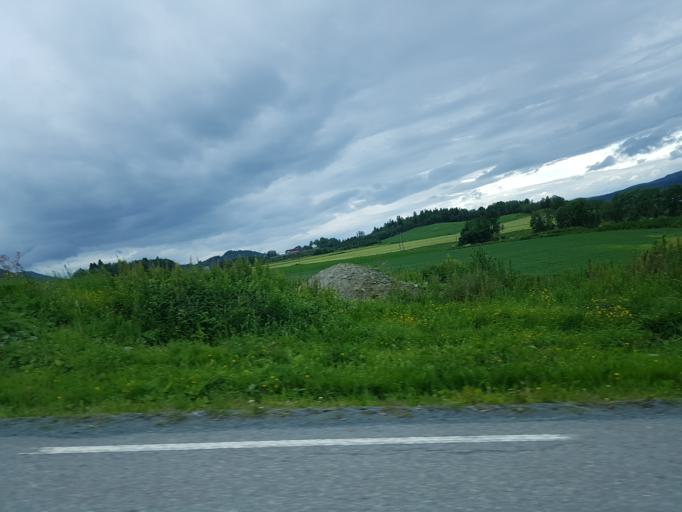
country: NO
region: Nord-Trondelag
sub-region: Levanger
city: Skogn
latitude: 63.6095
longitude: 11.0776
